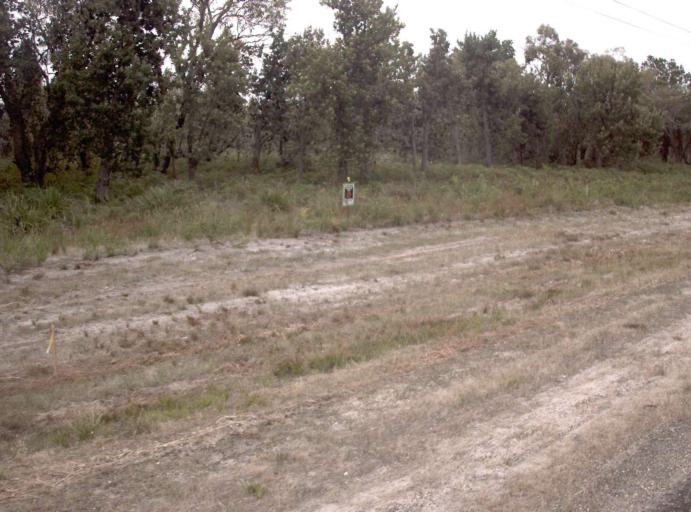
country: AU
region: Victoria
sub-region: East Gippsland
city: Bairnsdale
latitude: -38.0705
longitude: 147.5488
